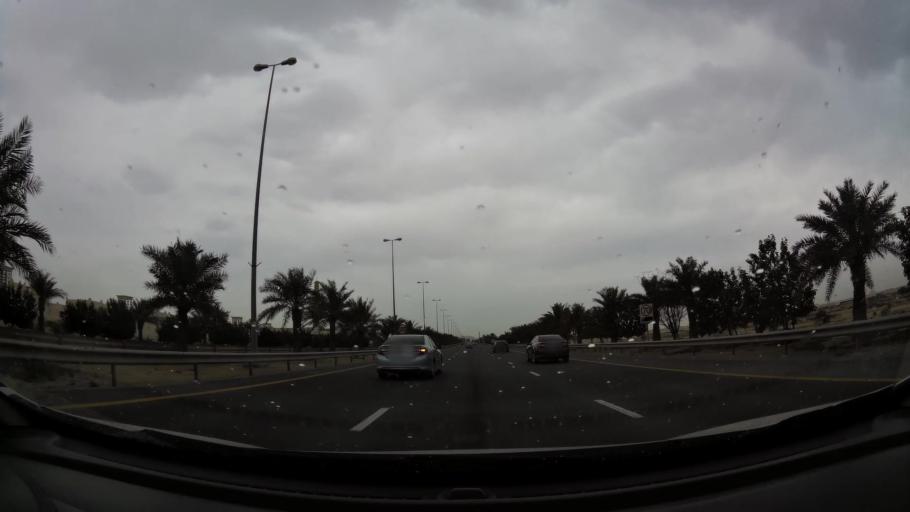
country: BH
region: Central Governorate
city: Dar Kulayb
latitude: 26.0897
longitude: 50.5393
